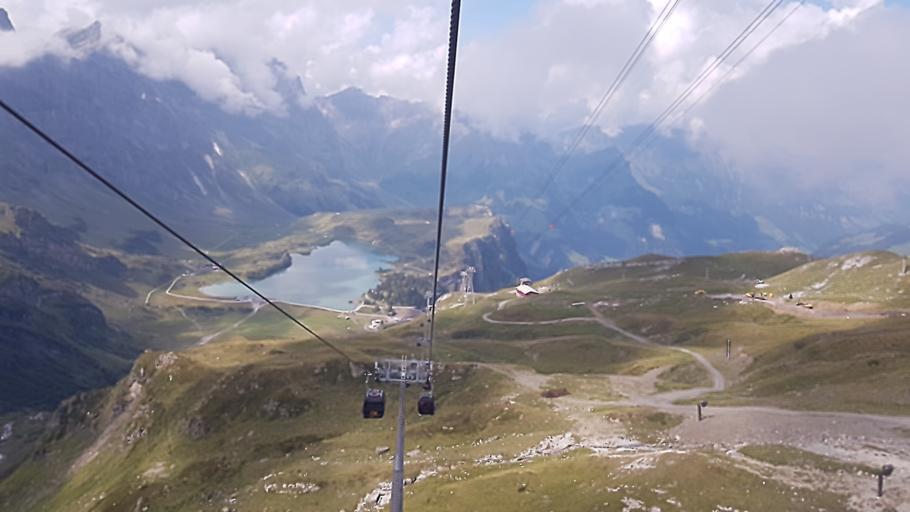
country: CH
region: Obwalden
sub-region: Obwalden
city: Engelberg
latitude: 46.7836
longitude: 8.4147
